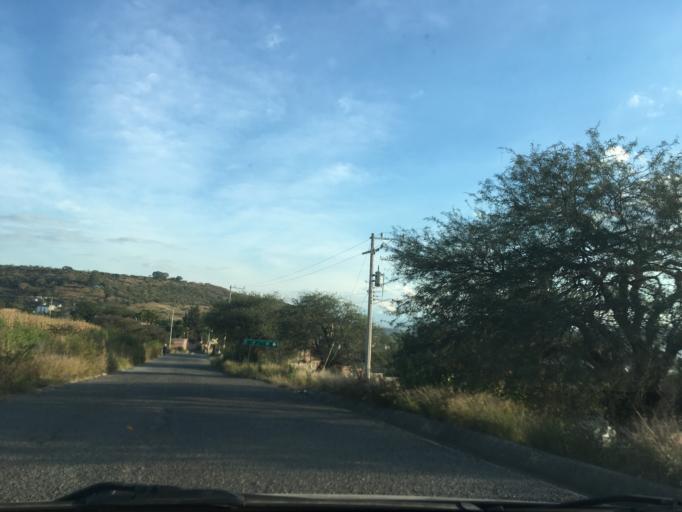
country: MX
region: Michoacan
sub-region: Cuitzeo
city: San Juan Benito Juarez (San Juan Tararameo)
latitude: 19.8756
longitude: -101.1437
